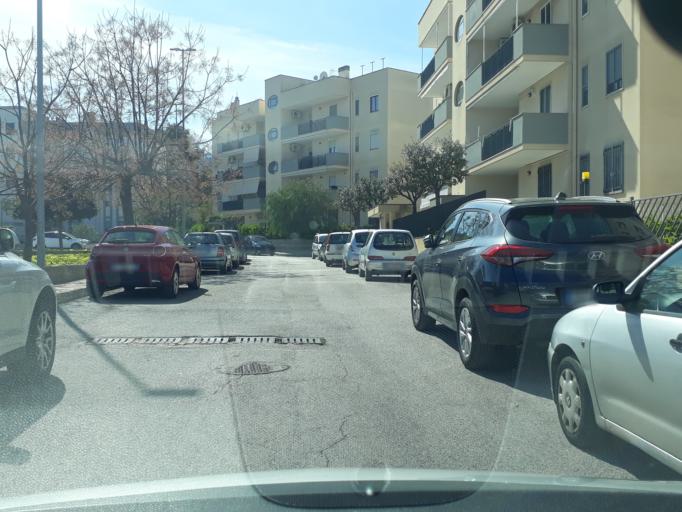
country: IT
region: Apulia
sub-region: Provincia di Brindisi
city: Fasano
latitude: 40.8380
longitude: 17.3529
